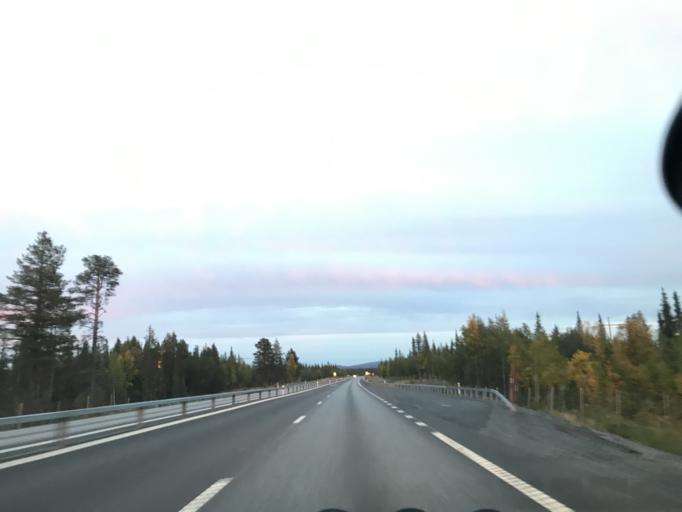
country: SE
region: Norrbotten
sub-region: Gallivare Kommun
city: Malmberget
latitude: 67.6907
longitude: 20.8336
